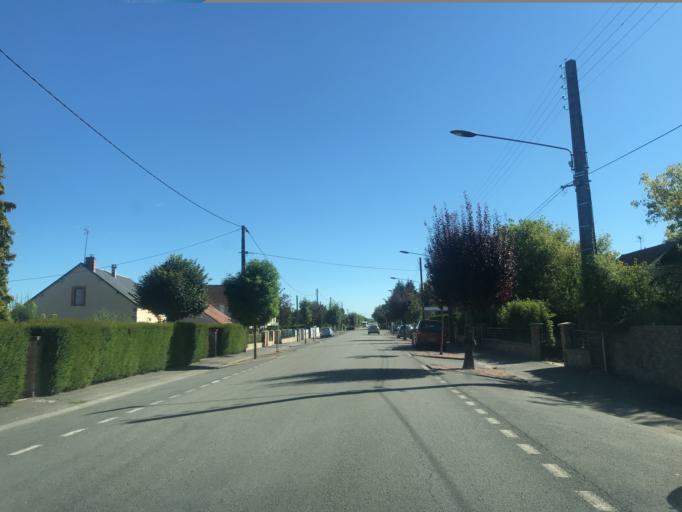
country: FR
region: Limousin
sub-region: Departement de la Creuse
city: Gouzon
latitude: 46.1942
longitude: 2.2448
